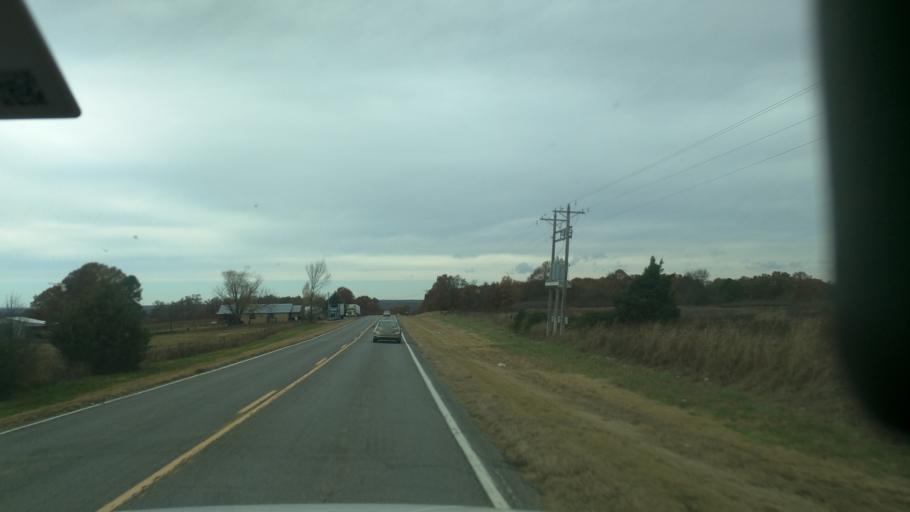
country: US
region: Oklahoma
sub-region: Cherokee County
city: Park Hill
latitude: 35.9024
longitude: -94.8189
